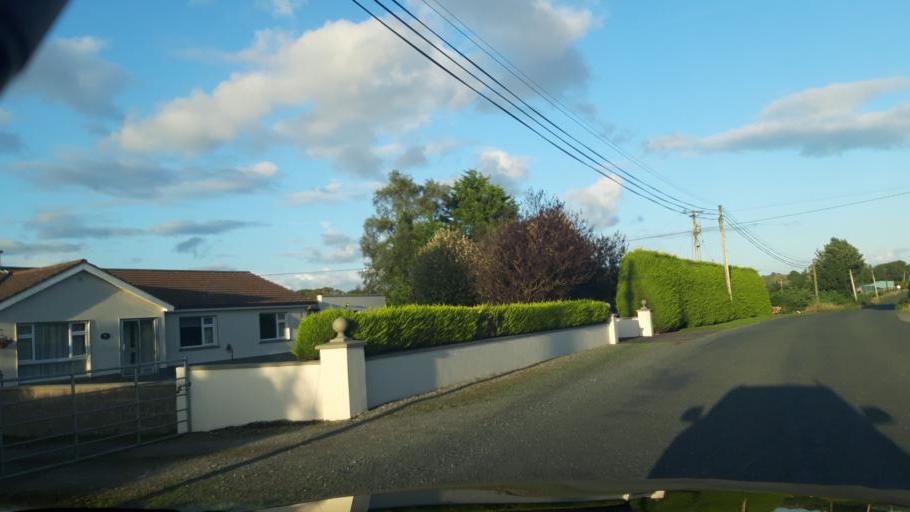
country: IE
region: Leinster
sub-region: An Iarmhi
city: Athlone
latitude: 53.4364
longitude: -7.8632
